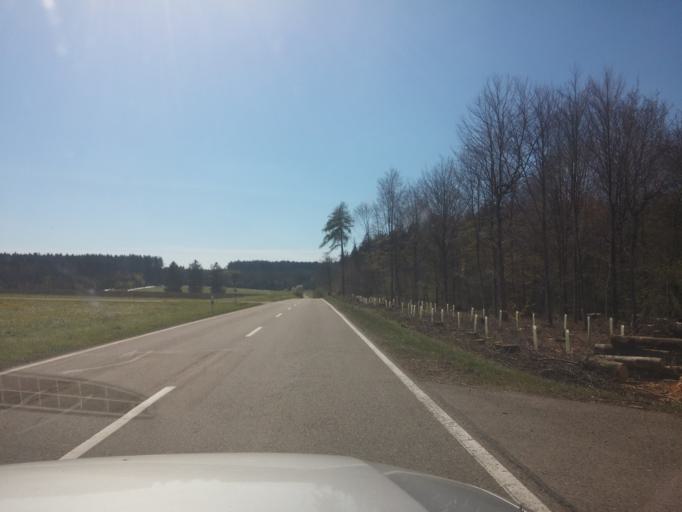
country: DE
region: Baden-Wuerttemberg
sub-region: Tuebingen Region
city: Aitrach
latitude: 47.9313
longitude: 10.0274
